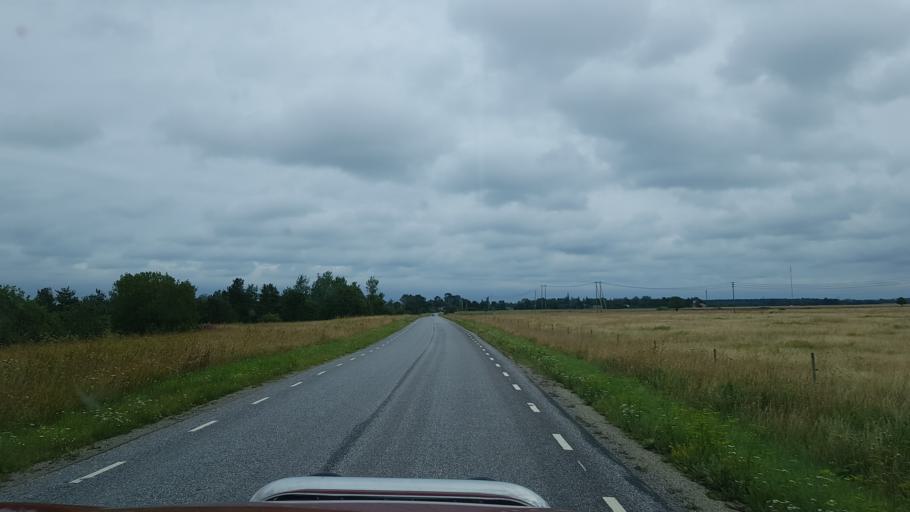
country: EE
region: Ida-Virumaa
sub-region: Puessi linn
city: Pussi
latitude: 59.3907
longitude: 27.0235
